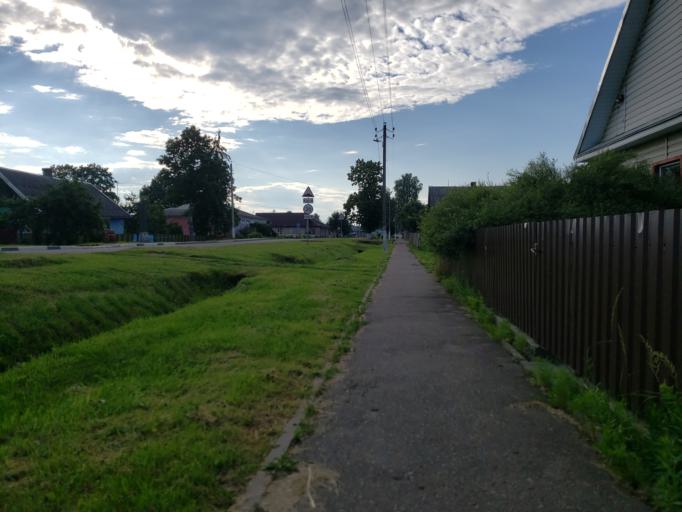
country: BY
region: Minsk
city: Chervyen'
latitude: 53.7073
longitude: 28.4321
